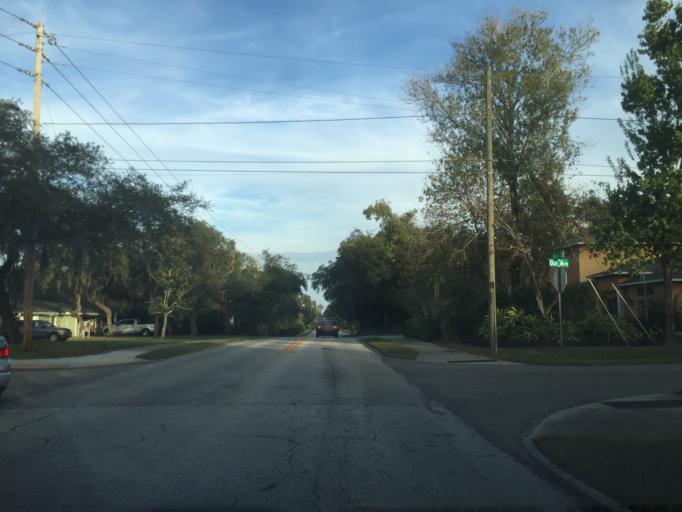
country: US
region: Florida
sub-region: Pinellas County
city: Safety Harbor
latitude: 27.9908
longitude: -82.7070
